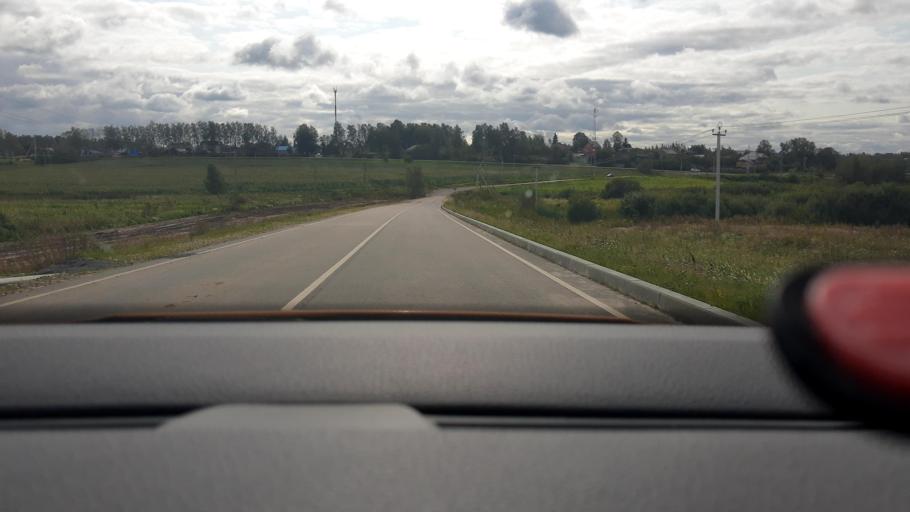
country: RU
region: Moskovskaya
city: Krasnoarmeysk
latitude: 56.0811
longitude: 38.0332
